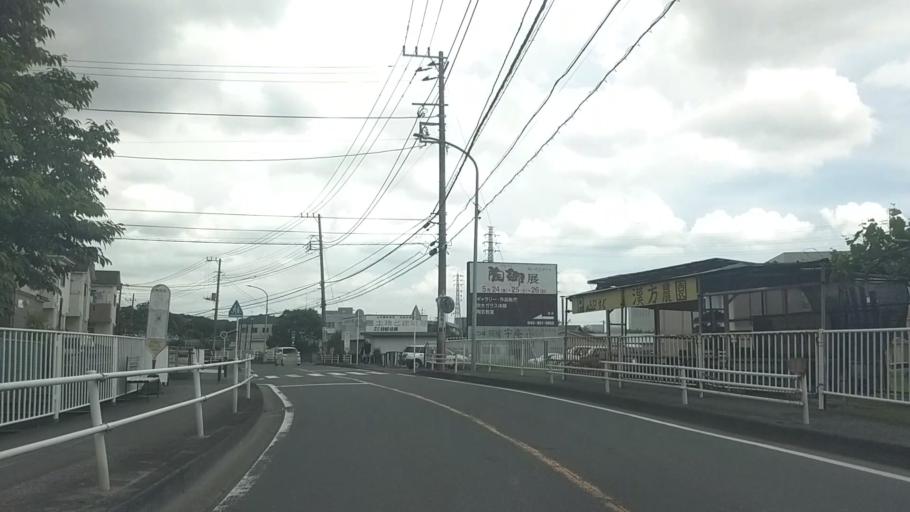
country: JP
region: Kanagawa
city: Fujisawa
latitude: 35.3670
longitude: 139.5226
